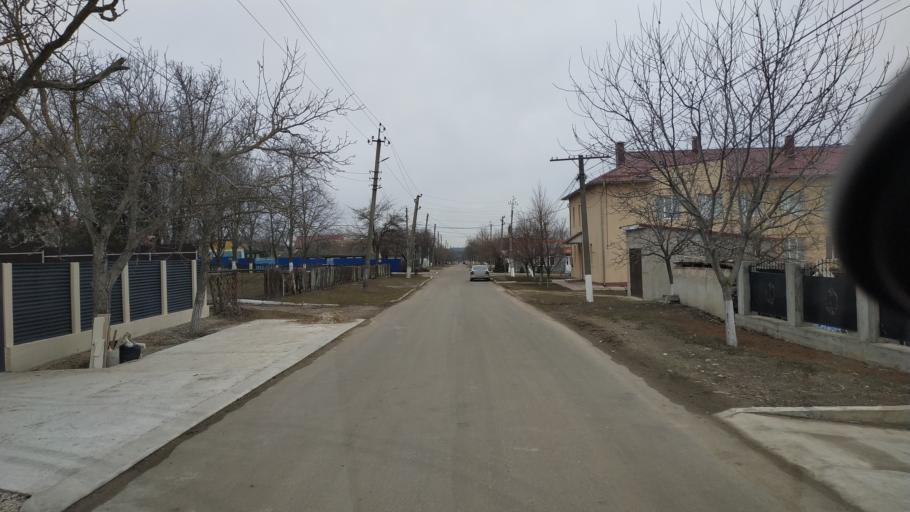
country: MD
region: Telenesti
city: Cocieri
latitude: 47.3120
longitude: 29.0695
